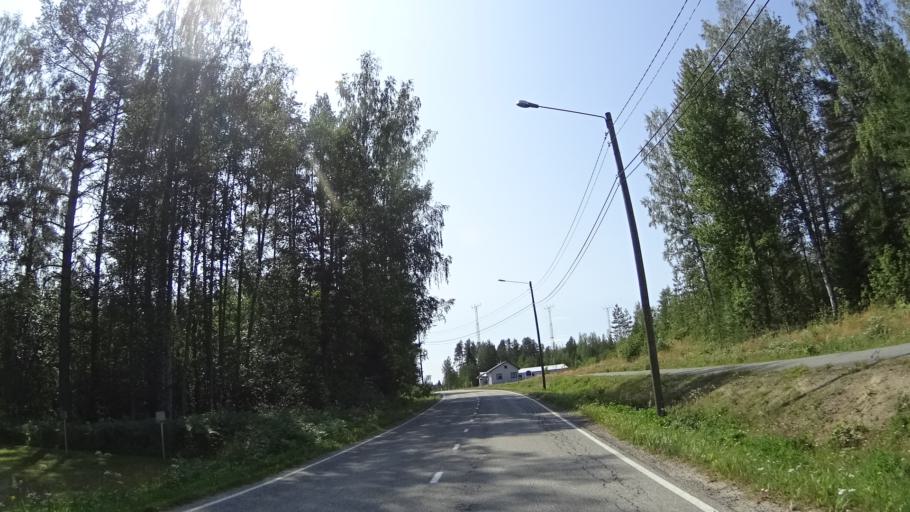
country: FI
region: Pirkanmaa
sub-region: Ylae-Pirkanmaa
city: Maenttae
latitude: 61.8582
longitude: 24.8235
